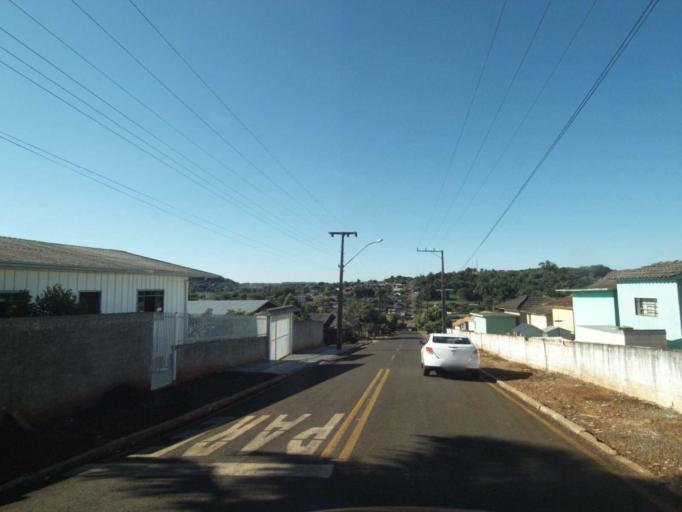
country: BR
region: Parana
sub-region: Coronel Vivida
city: Coronel Vivida
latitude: -25.9676
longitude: -52.8111
